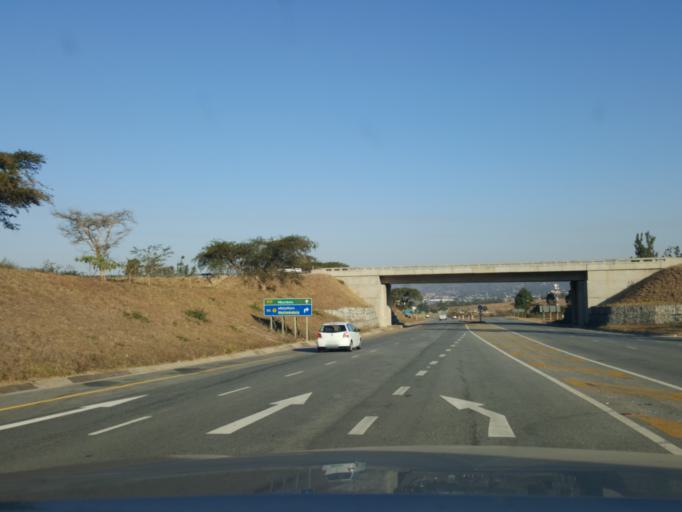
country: ZA
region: Mpumalanga
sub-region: Ehlanzeni District
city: Nelspruit
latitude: -25.4369
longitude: 30.9511
